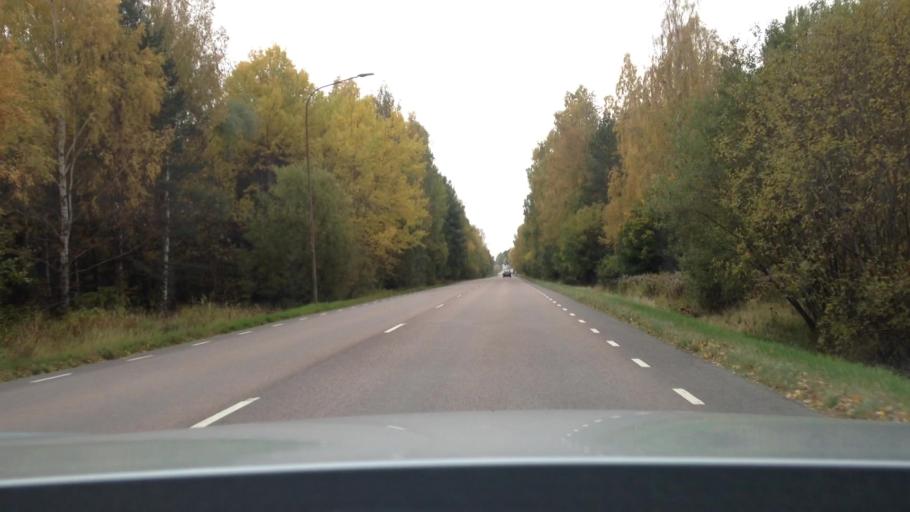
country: SE
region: Vaermland
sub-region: Karlstads Kommun
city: Karlstad
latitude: 59.3759
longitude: 13.4645
